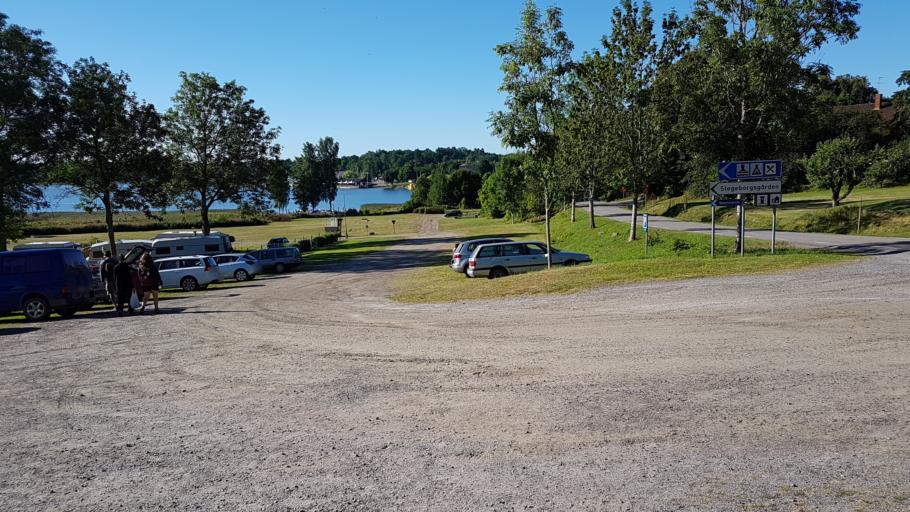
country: SE
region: OEstergoetland
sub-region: Valdemarsviks Kommun
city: Gusum
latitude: 58.4464
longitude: 16.5973
